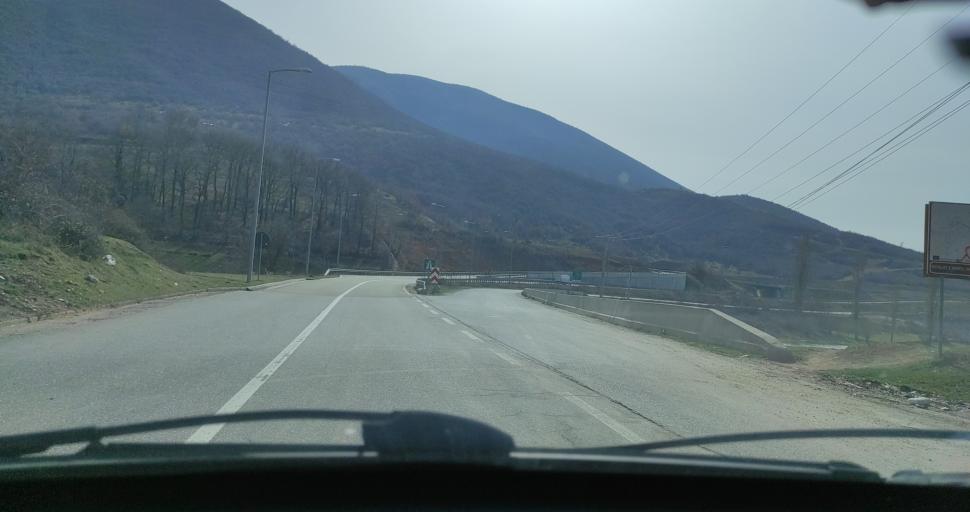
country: AL
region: Kukes
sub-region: Rrethi i Kukesit
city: Zapod
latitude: 42.1606
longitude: 20.5579
